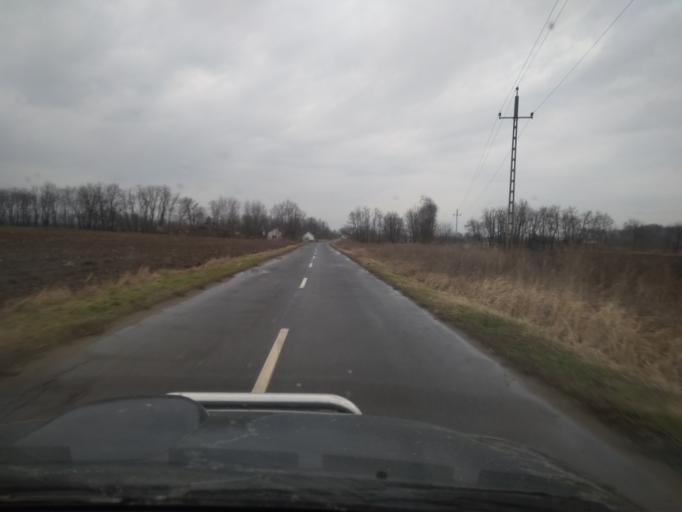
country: HU
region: Szabolcs-Szatmar-Bereg
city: Nyirtelek
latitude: 47.9663
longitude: 21.6475
